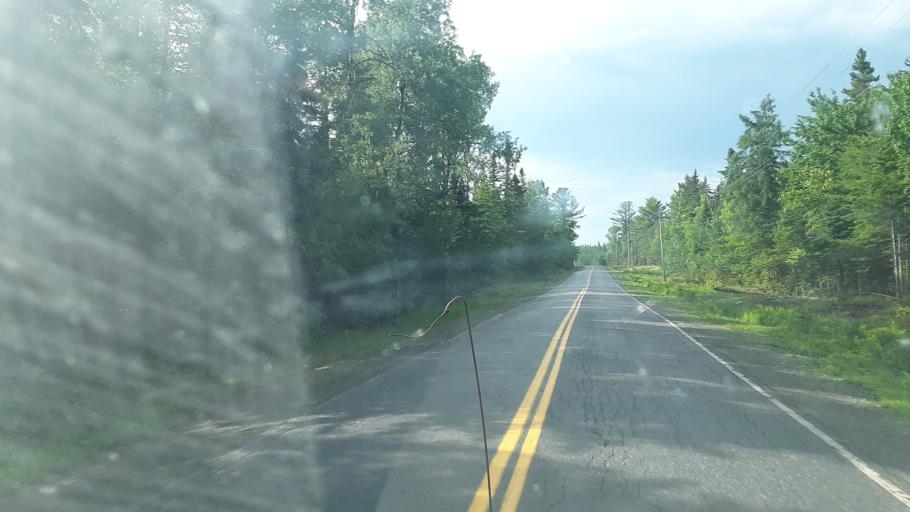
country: US
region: Maine
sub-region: Washington County
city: Calais
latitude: 45.1859
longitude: -67.5189
